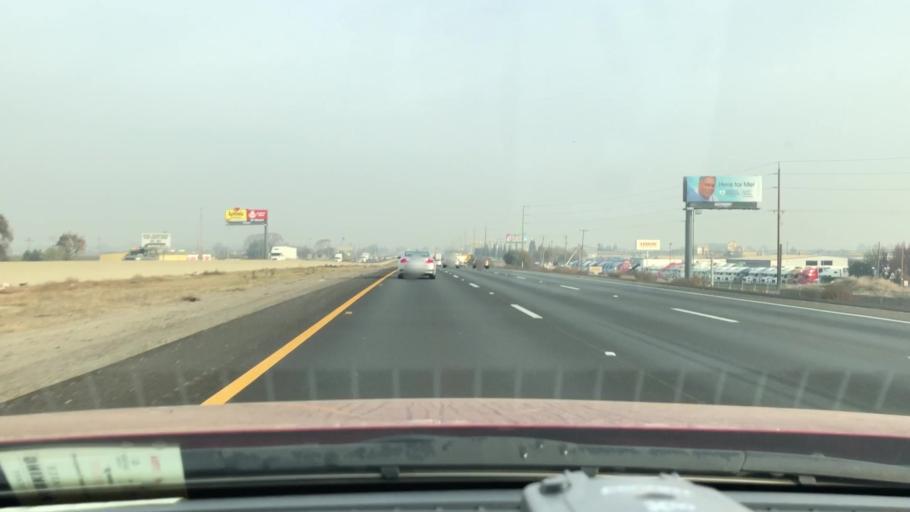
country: US
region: California
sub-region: San Joaquin County
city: French Camp
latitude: 37.8563
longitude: -121.2818
